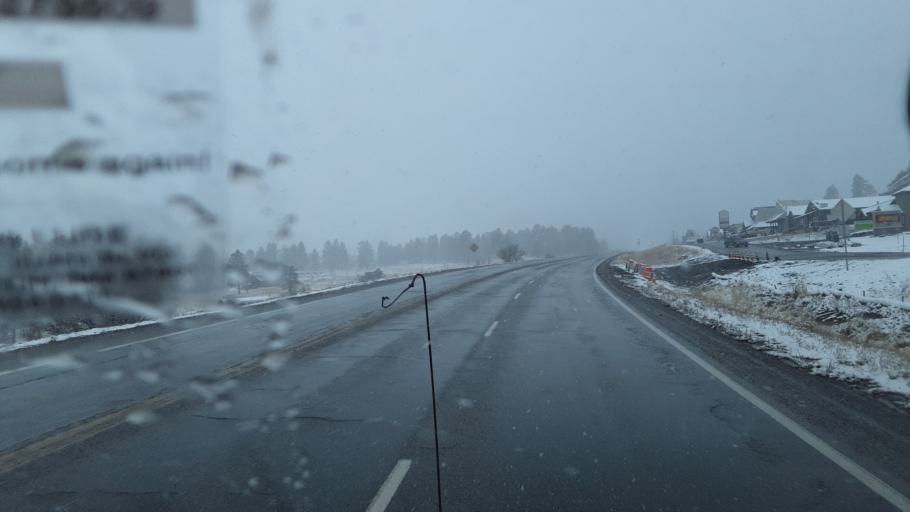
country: US
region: Colorado
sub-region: Archuleta County
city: Pagosa Springs
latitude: 37.2708
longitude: -107.0418
